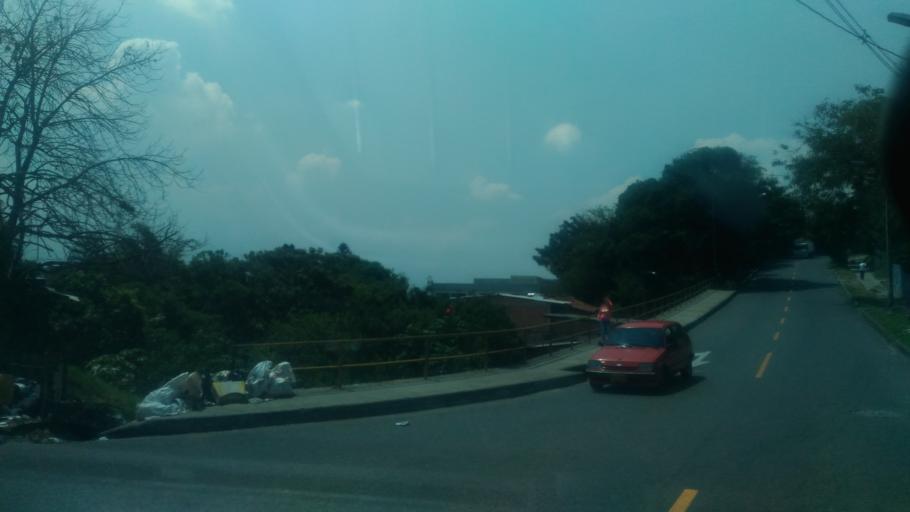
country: CO
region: Antioquia
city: Medellin
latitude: 6.2898
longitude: -75.5867
